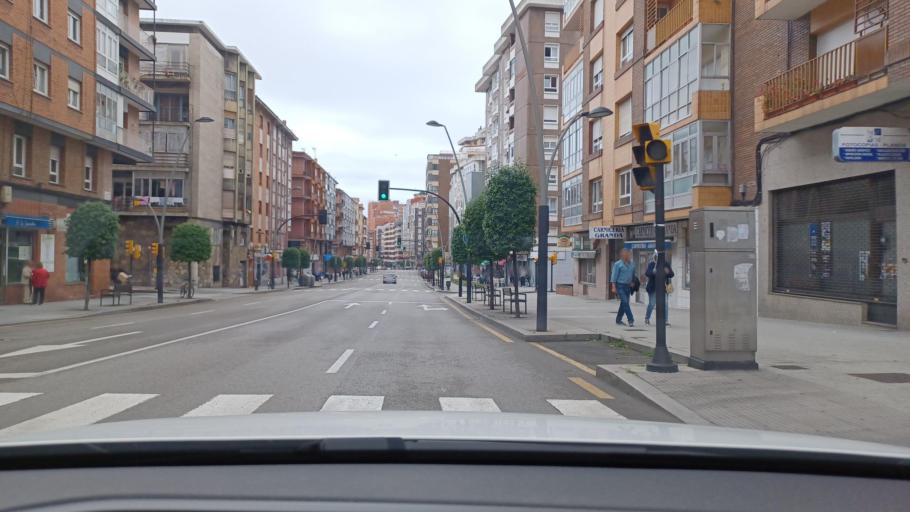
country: ES
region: Asturias
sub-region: Province of Asturias
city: Gijon
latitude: 43.5328
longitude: -5.6540
